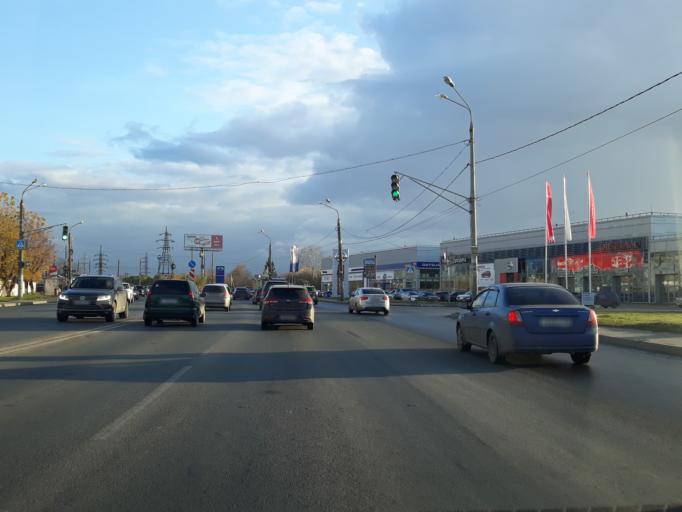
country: RU
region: Nizjnij Novgorod
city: Nizhniy Novgorod
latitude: 56.3106
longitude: 43.8996
